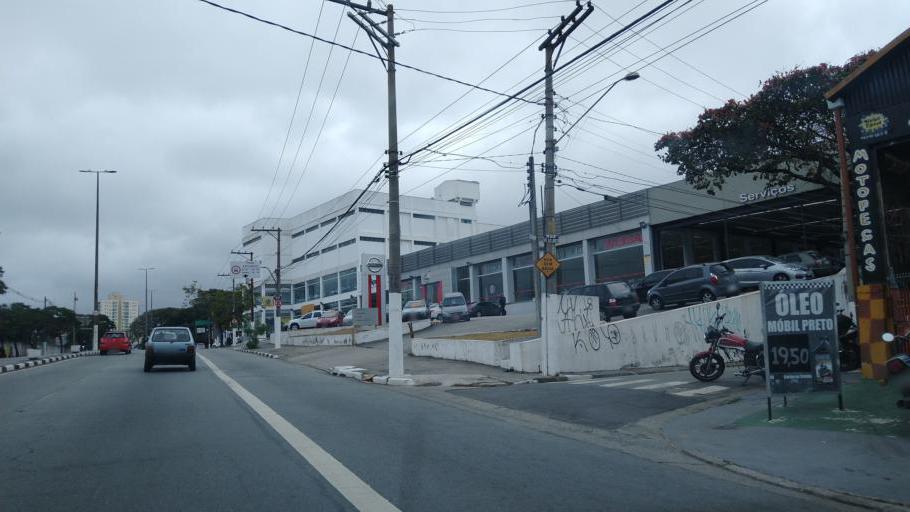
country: BR
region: Sao Paulo
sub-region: Osasco
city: Osasco
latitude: -23.5272
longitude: -46.7886
